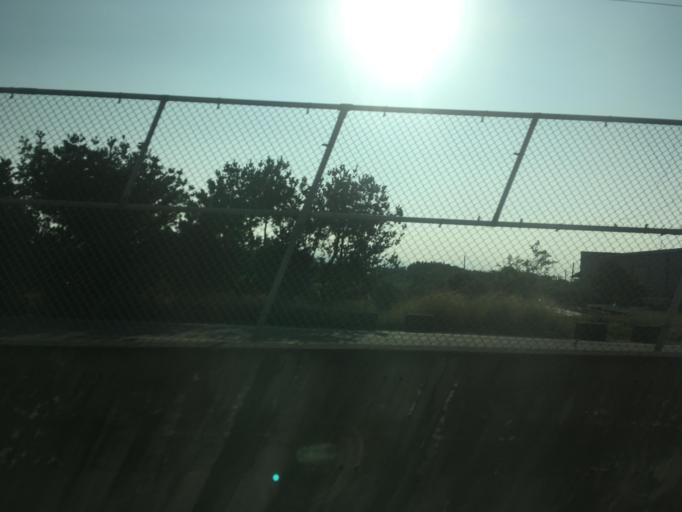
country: TW
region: Taiwan
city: Fengyuan
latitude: 24.2683
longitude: 120.6601
